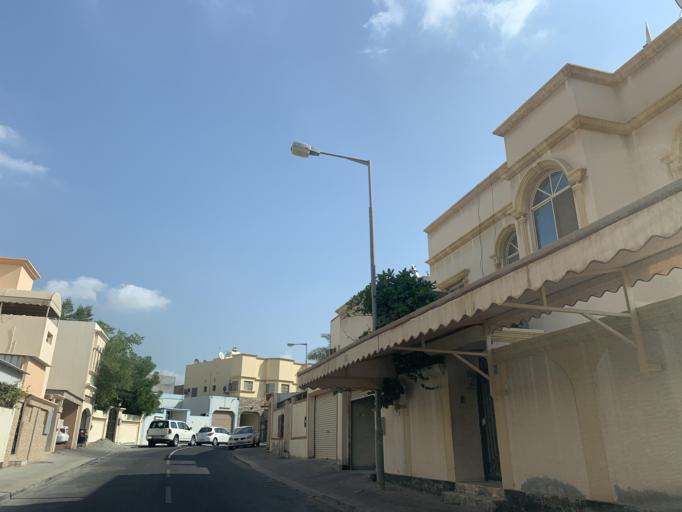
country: BH
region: Central Governorate
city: Madinat Hamad
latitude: 26.1361
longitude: 50.5024
